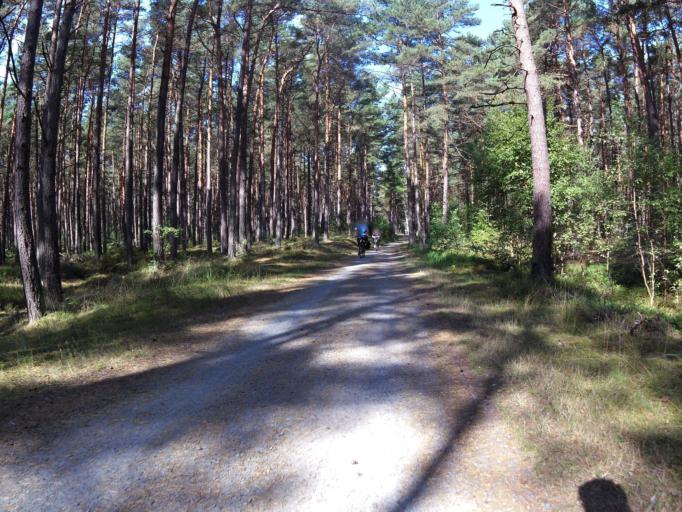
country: DE
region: Mecklenburg-Vorpommern
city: Karlshagen
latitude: 54.1053
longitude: 13.8539
